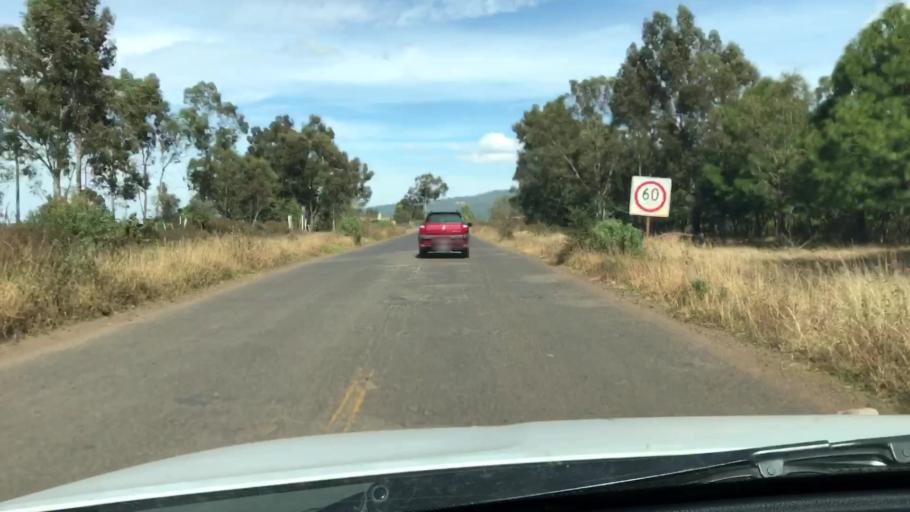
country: MX
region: Jalisco
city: Chiquilistlan
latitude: 20.1284
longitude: -103.7218
